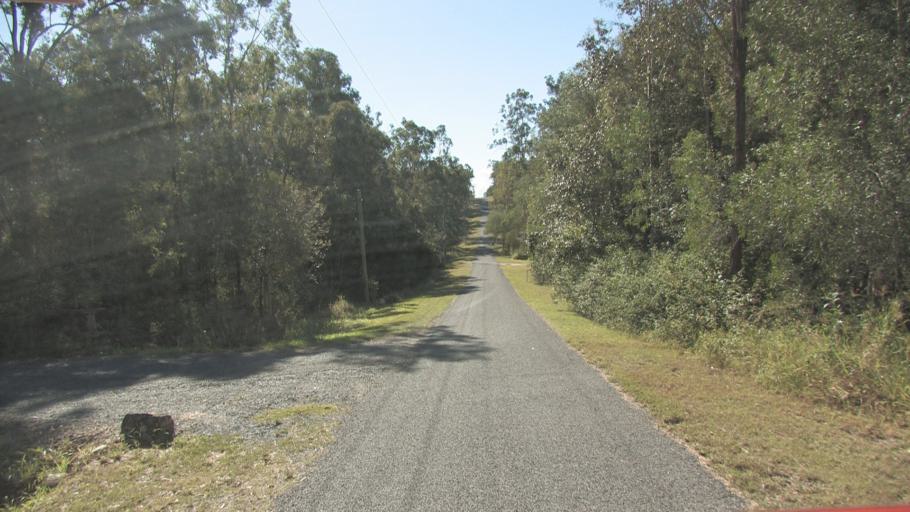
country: AU
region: Queensland
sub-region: Logan
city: Chambers Flat
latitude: -27.8193
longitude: 153.0768
